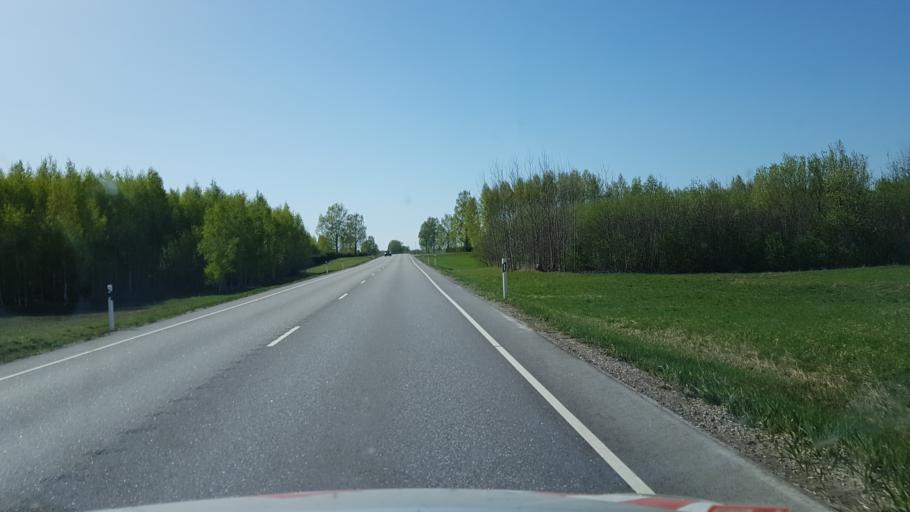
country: EE
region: Viljandimaa
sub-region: Abja vald
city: Abja-Paluoja
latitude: 58.1175
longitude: 25.4206
